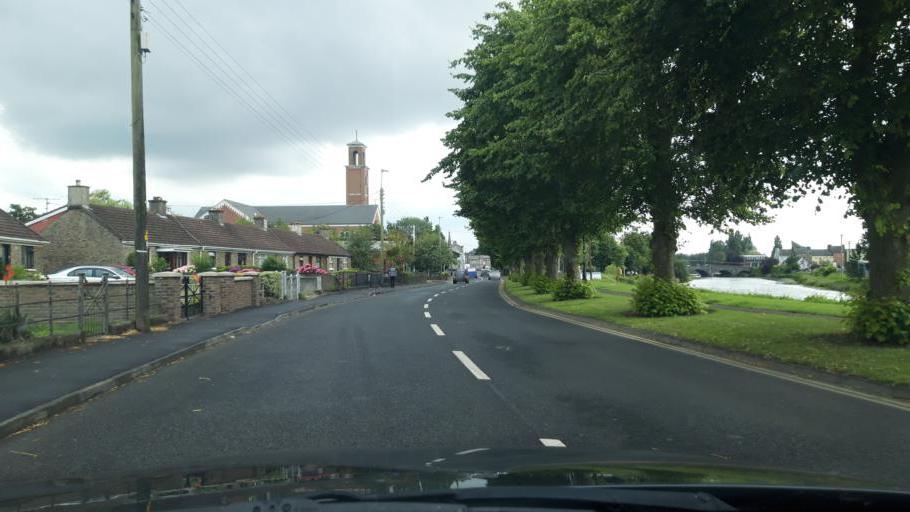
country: IE
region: Leinster
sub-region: Kildare
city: Athy
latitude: 52.9953
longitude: -6.9847
